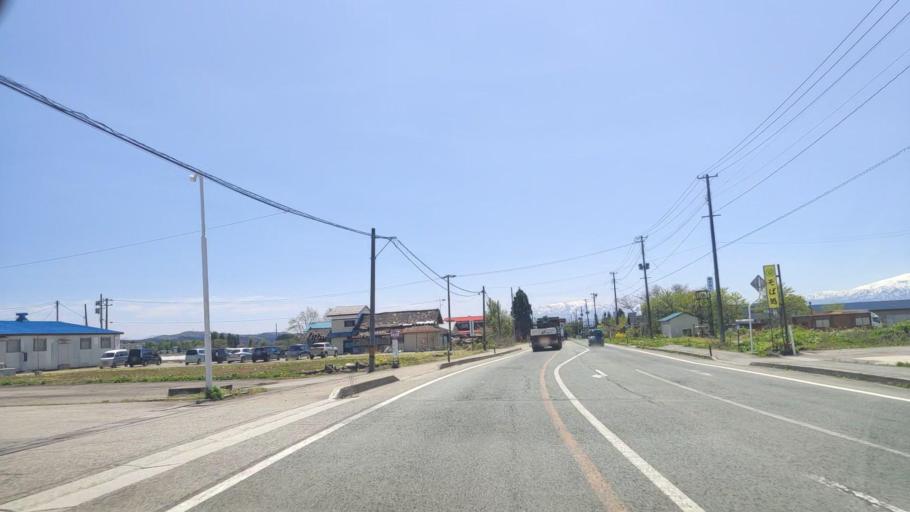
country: JP
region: Yamagata
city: Shinjo
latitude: 38.8201
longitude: 140.3265
